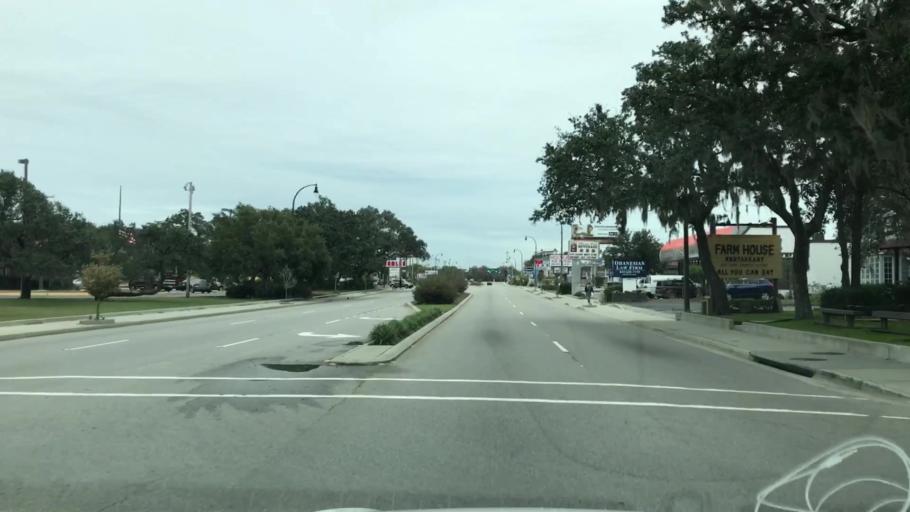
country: US
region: South Carolina
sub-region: Horry County
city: Myrtle Beach
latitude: 33.6898
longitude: -78.8867
